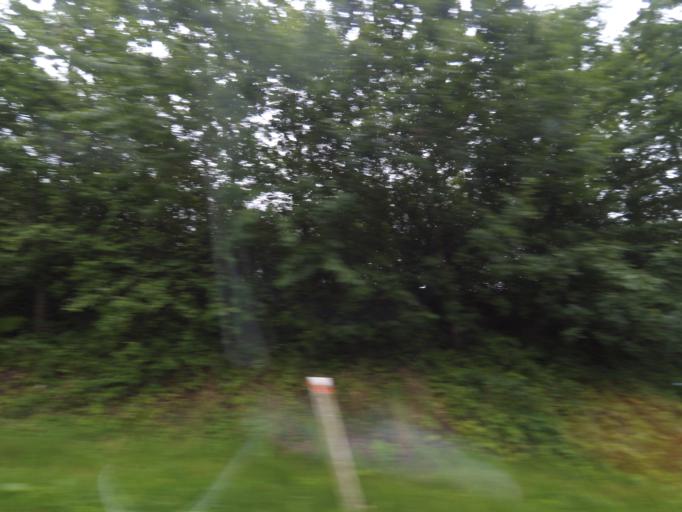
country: DK
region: South Denmark
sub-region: Middelfart Kommune
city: Norre Aby
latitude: 55.4716
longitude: 9.8963
